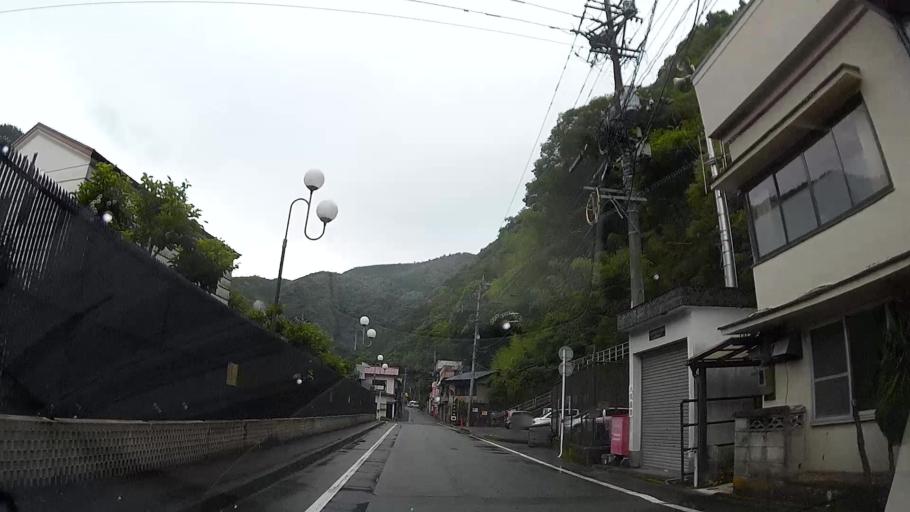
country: JP
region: Oita
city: Tsukawaki
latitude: 33.1822
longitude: 131.0358
